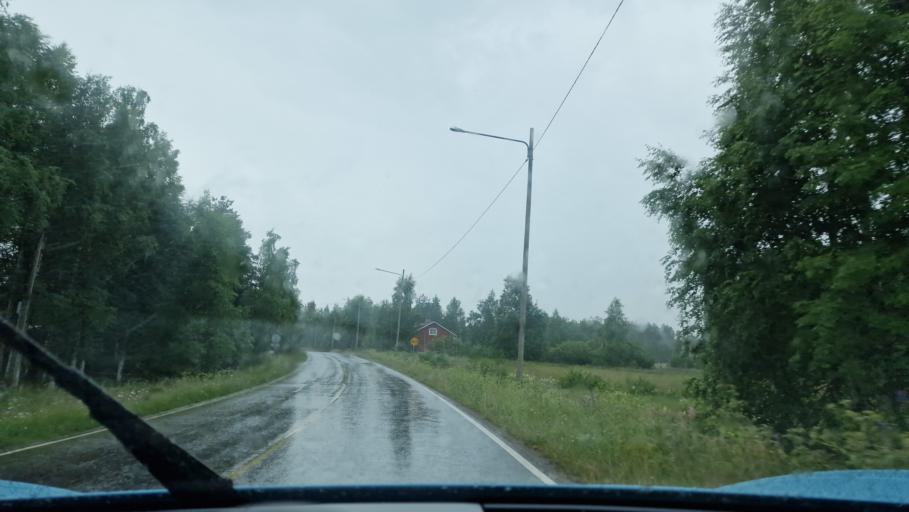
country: FI
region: Southern Ostrobothnia
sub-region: Jaerviseutu
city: Soini
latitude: 62.8441
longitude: 24.3255
